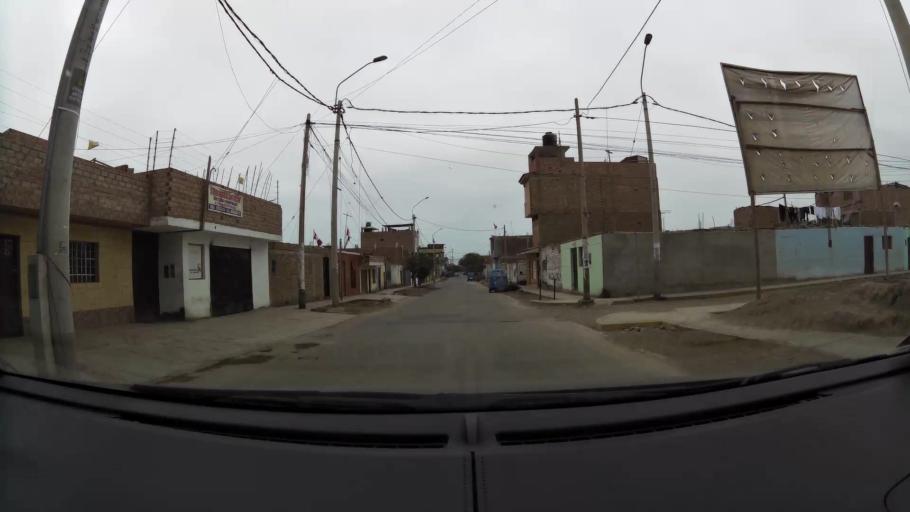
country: PE
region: Lima
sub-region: Barranca
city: Barranca
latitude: -10.7447
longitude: -77.7564
